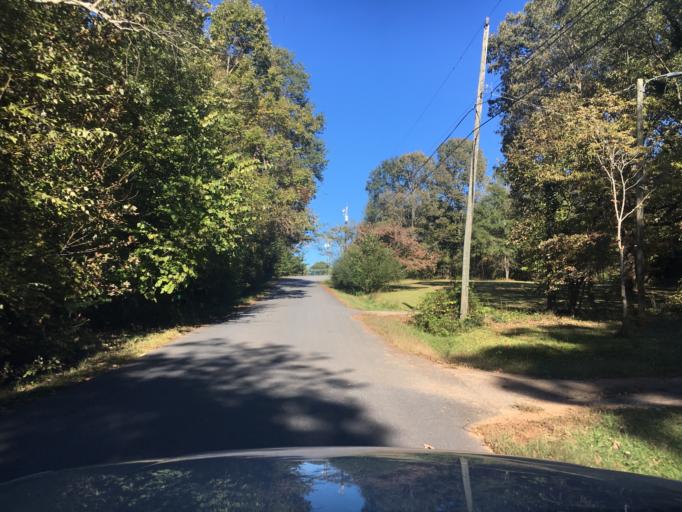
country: US
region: South Carolina
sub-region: Spartanburg County
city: Lyman
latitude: 34.9162
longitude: -82.1145
